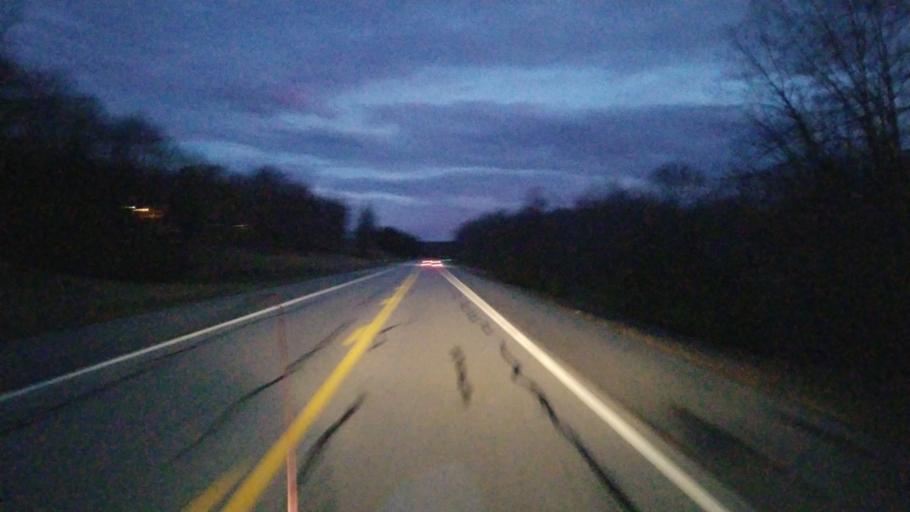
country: US
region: Tennessee
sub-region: Sequatchie County
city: Dunlap
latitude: 35.4991
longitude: -85.4736
